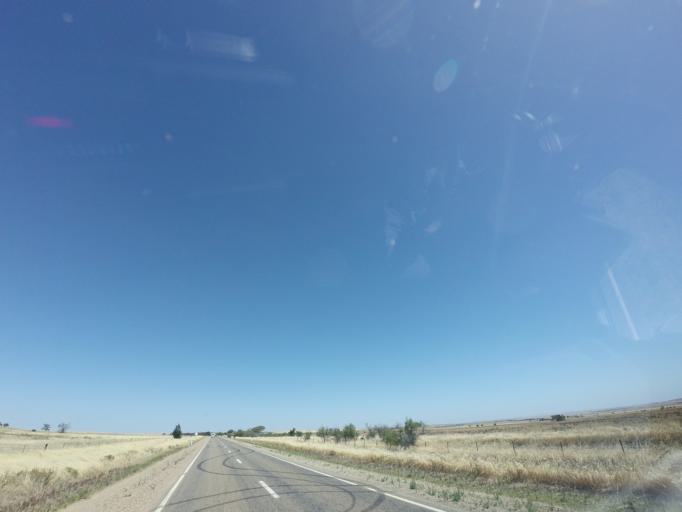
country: AU
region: South Australia
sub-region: Peterborough
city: Peterborough
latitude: -32.9526
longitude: 138.7920
